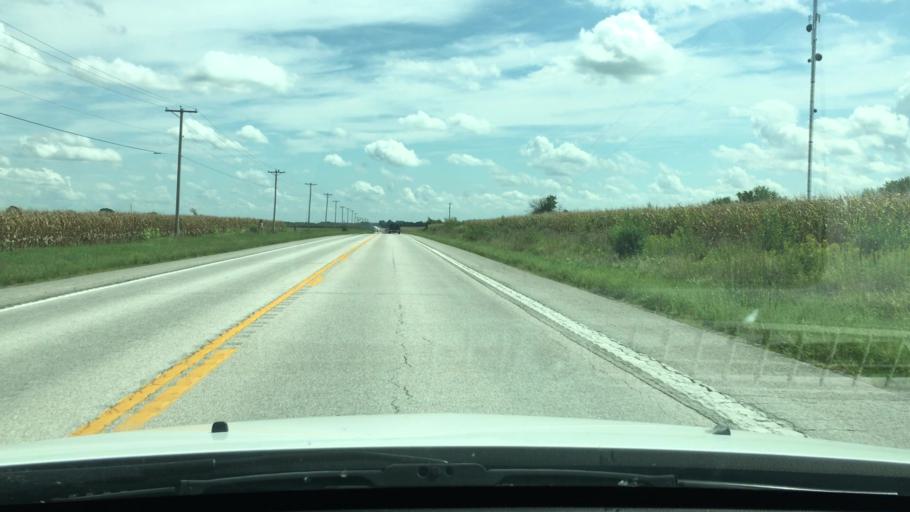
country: US
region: Missouri
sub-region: Pike County
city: Bowling Green
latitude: 39.3447
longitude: -91.3088
